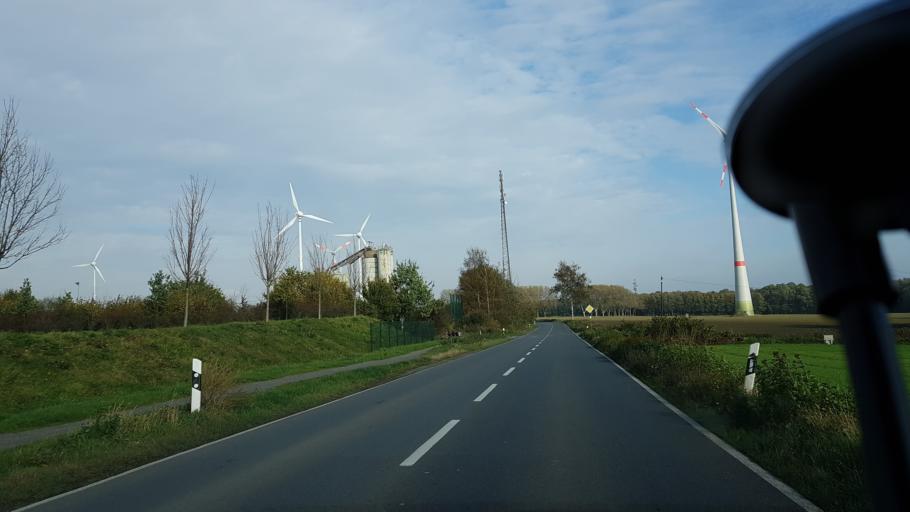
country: DE
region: North Rhine-Westphalia
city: Castrop-Rauxel
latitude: 51.5415
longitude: 7.3400
